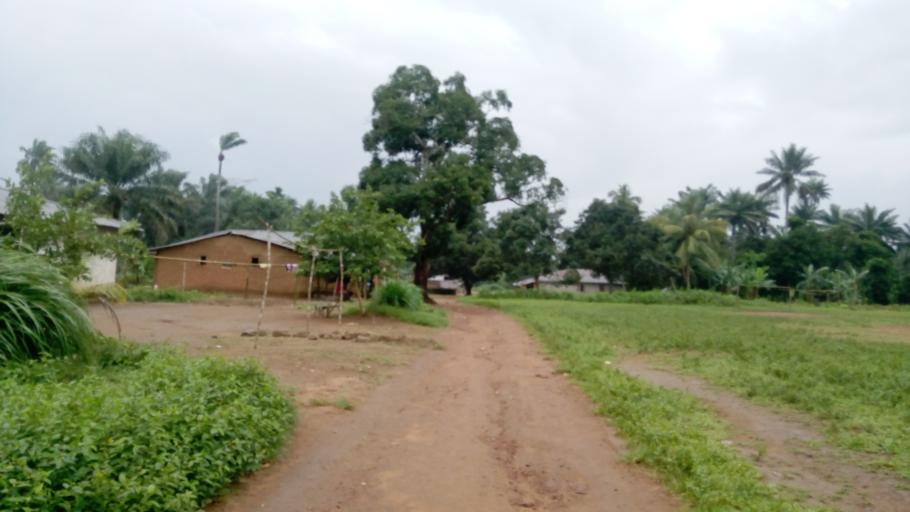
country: SL
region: Northern Province
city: Port Loko
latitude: 8.4999
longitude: -12.7511
